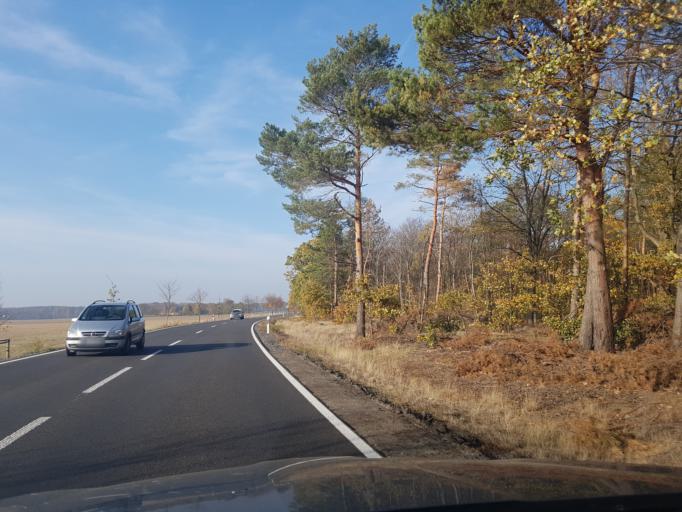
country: DE
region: Saxony
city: Arzberg
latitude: 51.5511
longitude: 13.1237
